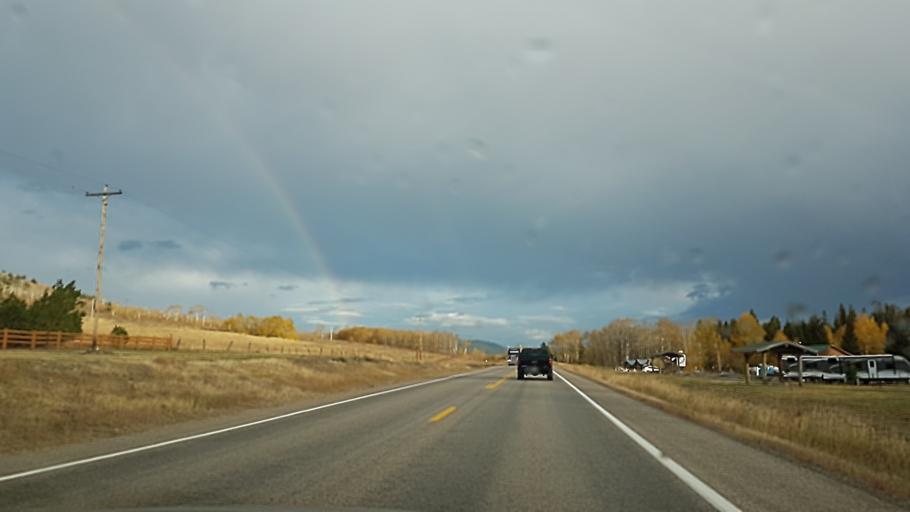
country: US
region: Montana
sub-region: Gallatin County
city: West Yellowstone
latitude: 44.6703
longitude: -111.4015
